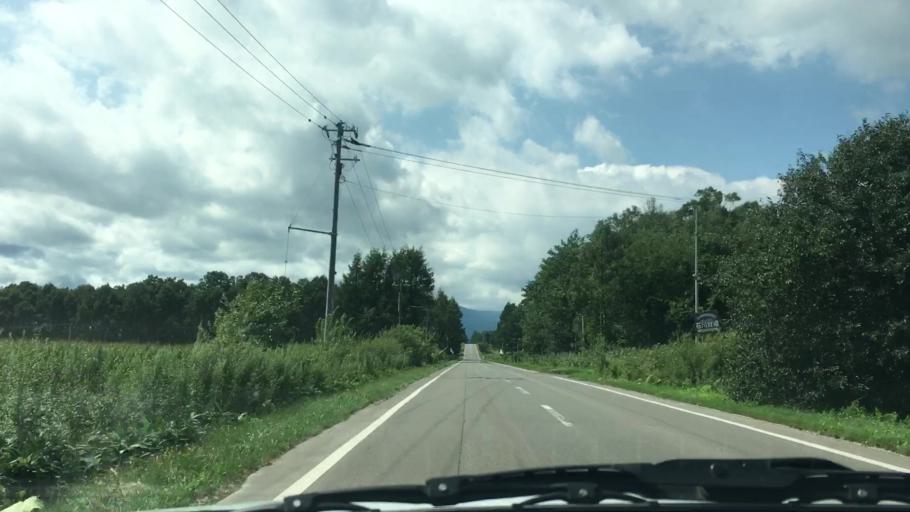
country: JP
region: Hokkaido
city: Otofuke
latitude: 43.2767
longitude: 143.3695
